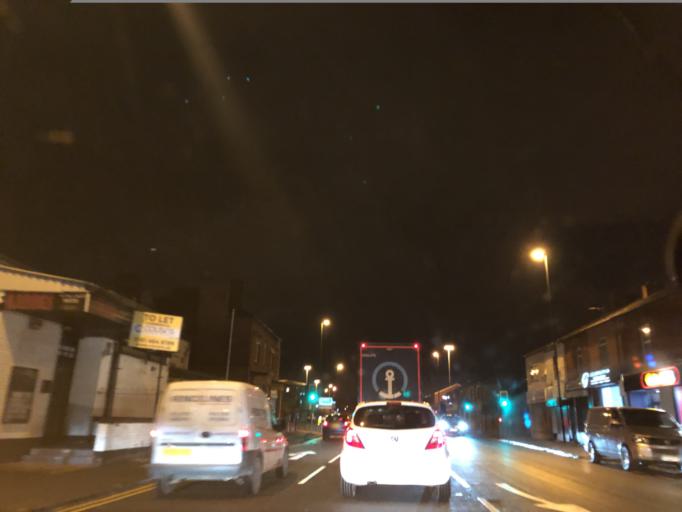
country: GB
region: England
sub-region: Manchester
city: Failsworth
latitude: 53.5170
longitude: -2.1477
